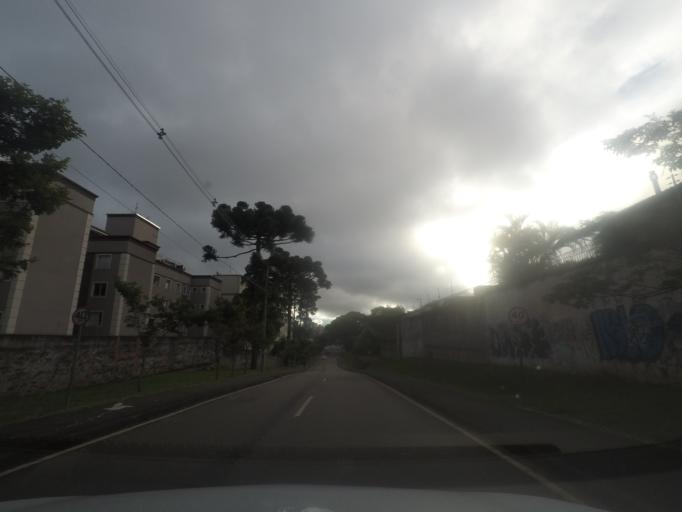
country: BR
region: Parana
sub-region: Curitiba
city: Curitiba
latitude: -25.4330
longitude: -49.2446
